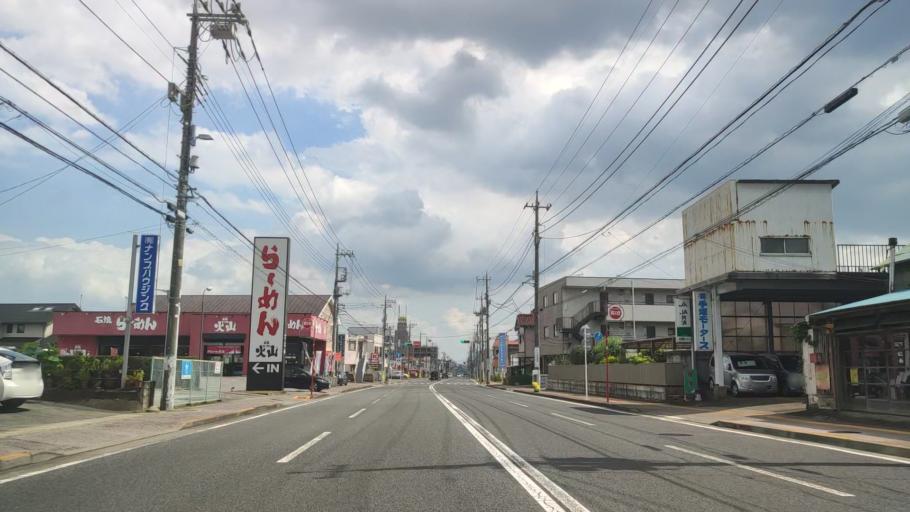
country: JP
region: Tochigi
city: Utsunomiya-shi
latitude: 36.5842
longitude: 139.8671
